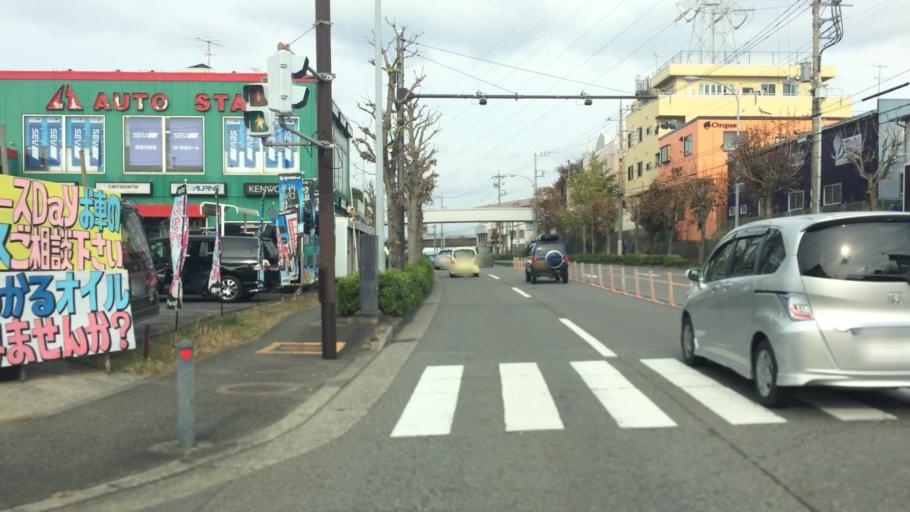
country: JP
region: Kanagawa
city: Yokohama
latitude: 35.5436
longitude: 139.6005
